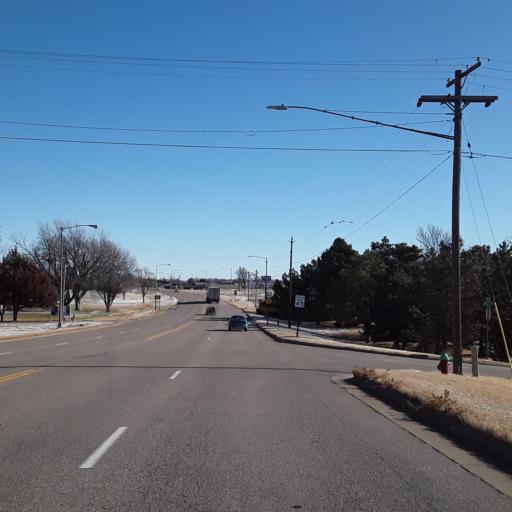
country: US
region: Kansas
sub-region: Pawnee County
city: Larned
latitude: 38.1882
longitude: -99.0920
